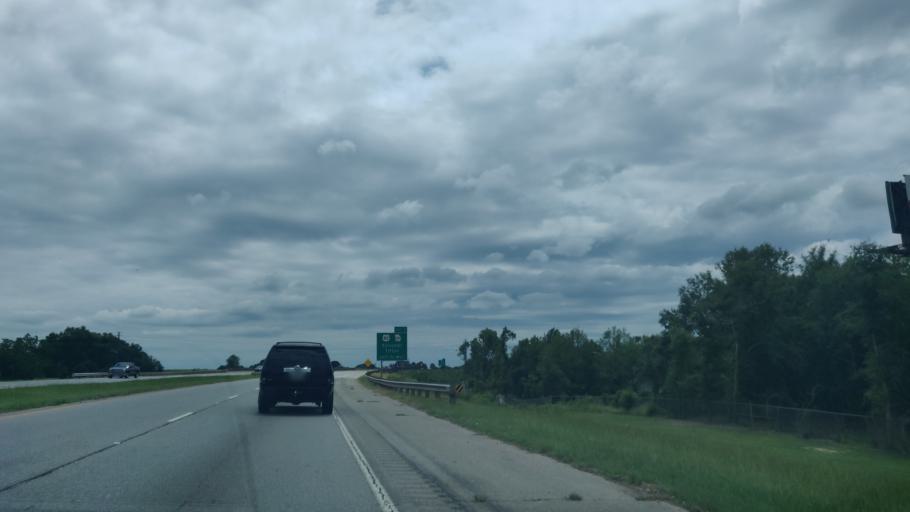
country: US
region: Georgia
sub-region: Dougherty County
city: Albany
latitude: 31.5896
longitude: -84.1178
